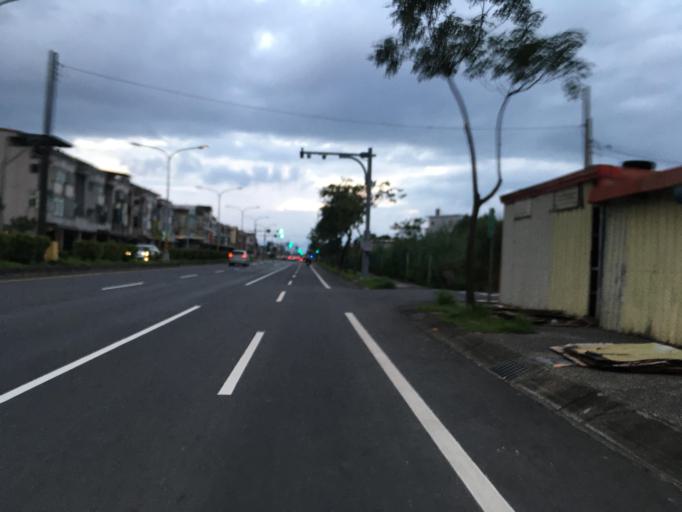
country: TW
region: Taiwan
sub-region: Yilan
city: Yilan
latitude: 24.6207
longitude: 121.8418
